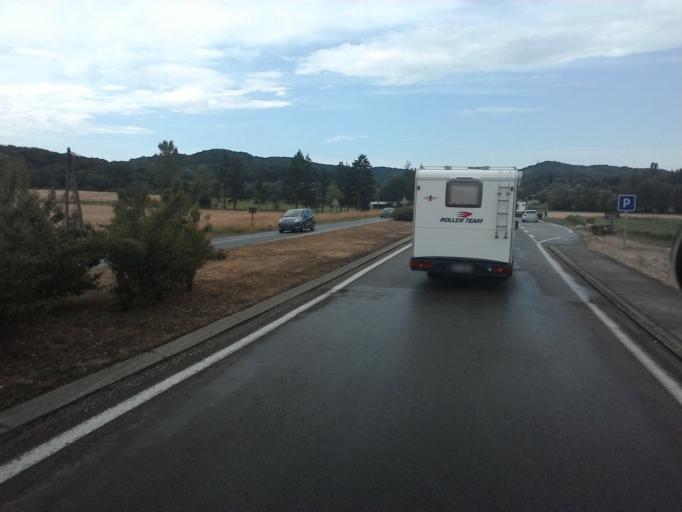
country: FR
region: Franche-Comte
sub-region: Departement du Jura
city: Poligny
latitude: 46.8107
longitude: 5.5851
